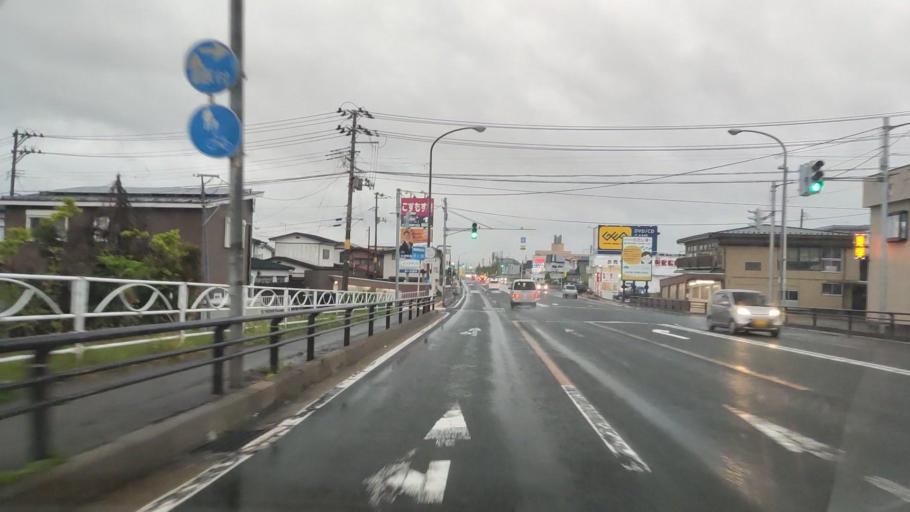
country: JP
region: Akita
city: Akita
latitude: 39.6954
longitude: 140.1197
